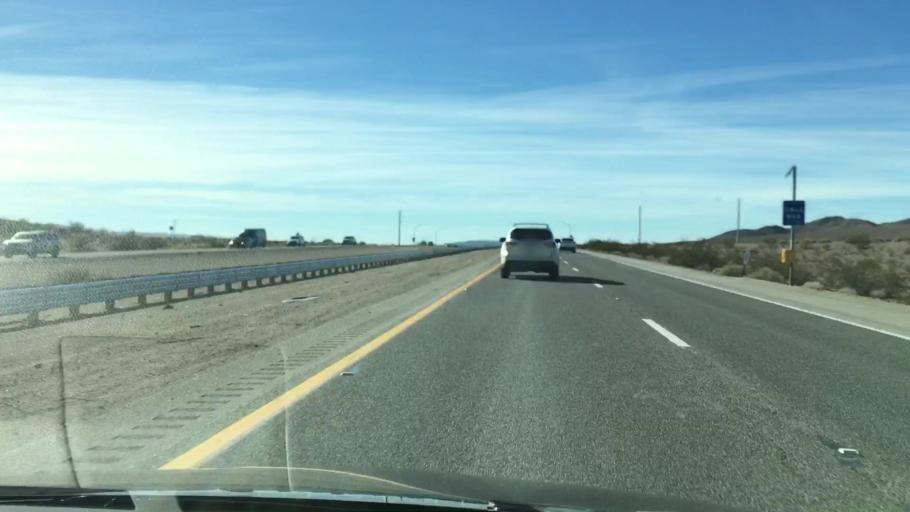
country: US
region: California
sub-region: San Bernardino County
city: Barstow
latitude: 34.9183
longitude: -116.7718
